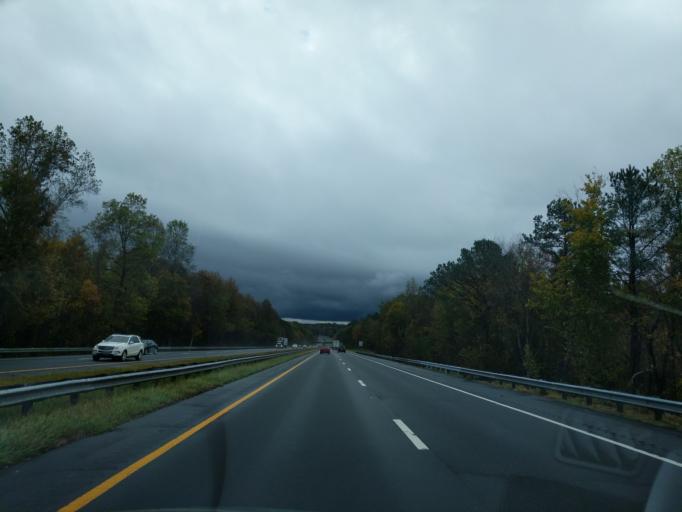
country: US
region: North Carolina
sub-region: Orange County
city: Hillsborough
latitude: 36.0443
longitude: -79.0399
